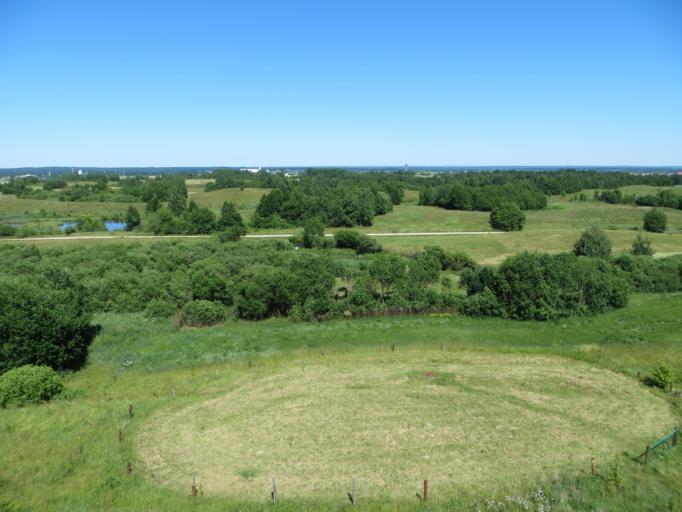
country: LT
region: Vilnius County
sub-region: Vilniaus Rajonas
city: Vievis
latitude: 54.7596
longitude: 24.7548
